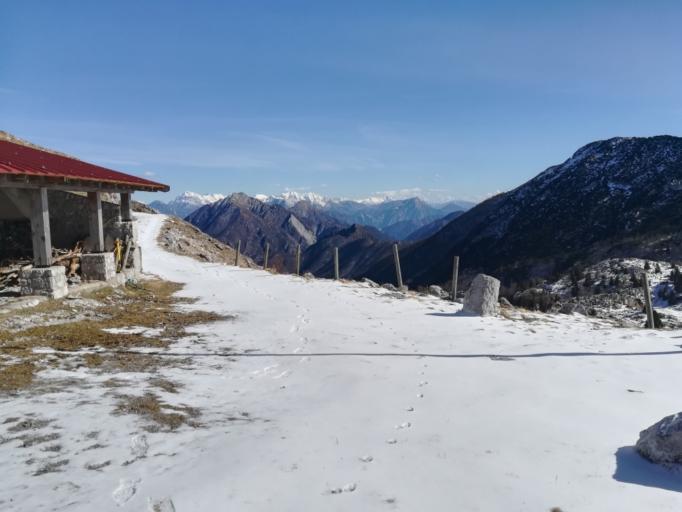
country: IT
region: Friuli Venezia Giulia
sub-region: Provincia di Udine
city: Preone
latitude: 46.3358
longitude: 12.8463
